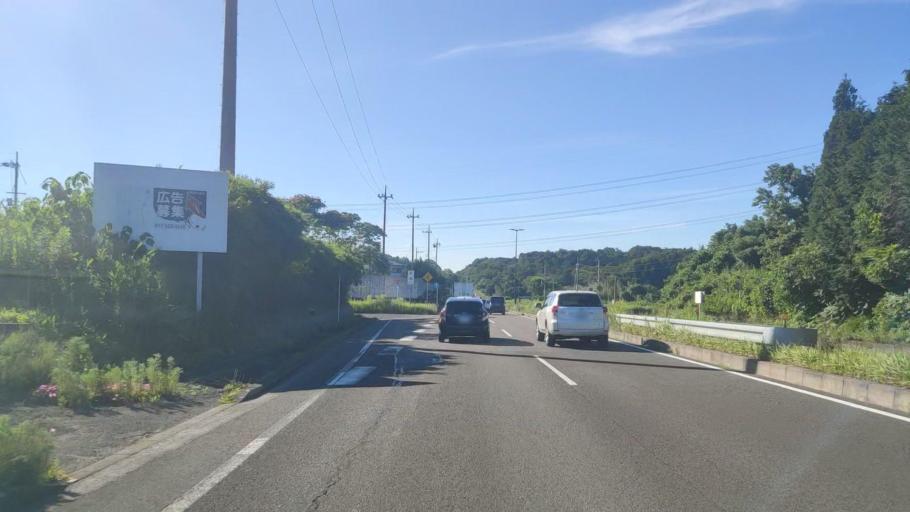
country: JP
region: Shiga Prefecture
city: Minakuchicho-matoba
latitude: 34.9657
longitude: 136.1967
